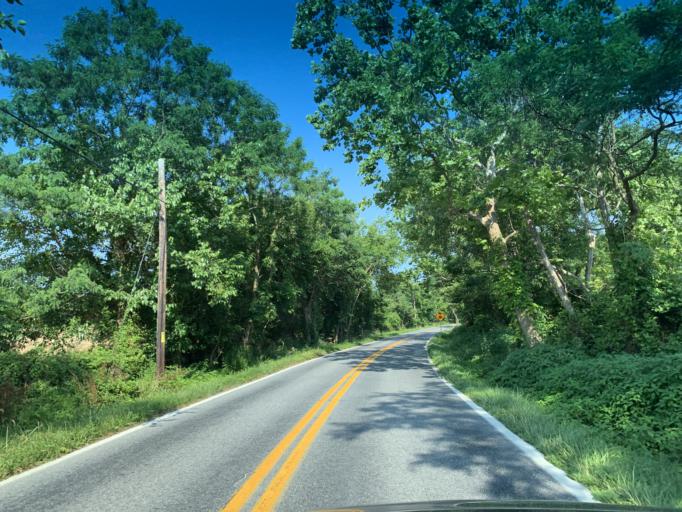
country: US
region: Maryland
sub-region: Montgomery County
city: Clarksburg
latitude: 39.2480
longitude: -77.3525
